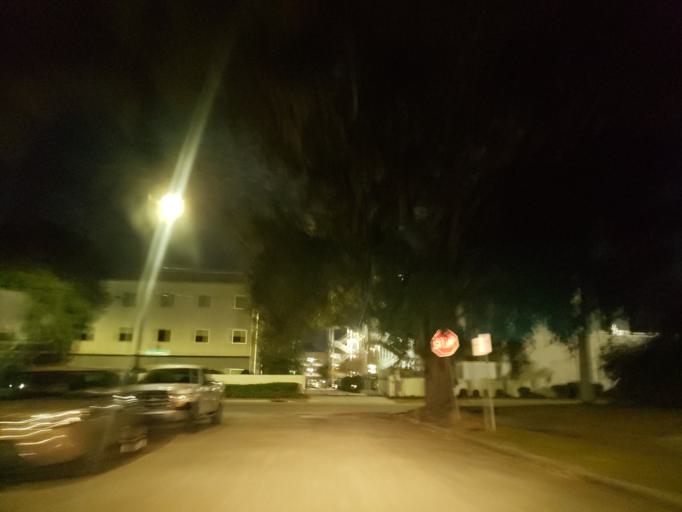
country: US
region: Georgia
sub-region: Chatham County
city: Savannah
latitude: 32.0476
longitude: -81.1081
